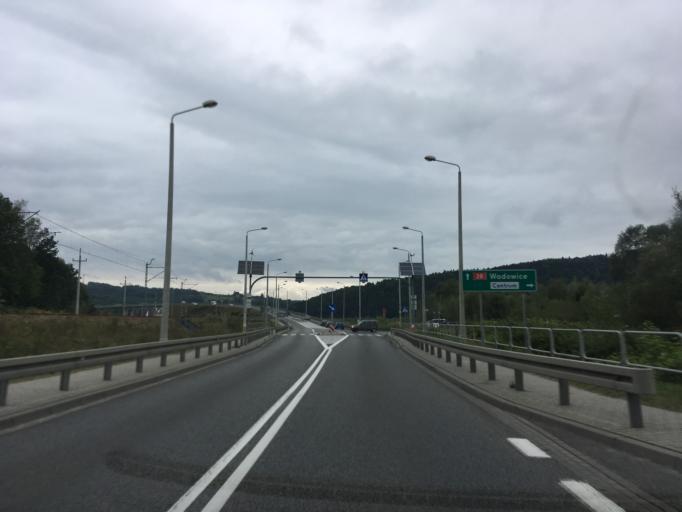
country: PL
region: Lesser Poland Voivodeship
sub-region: Powiat suski
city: Zembrzyce
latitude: 49.7764
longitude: 19.5912
